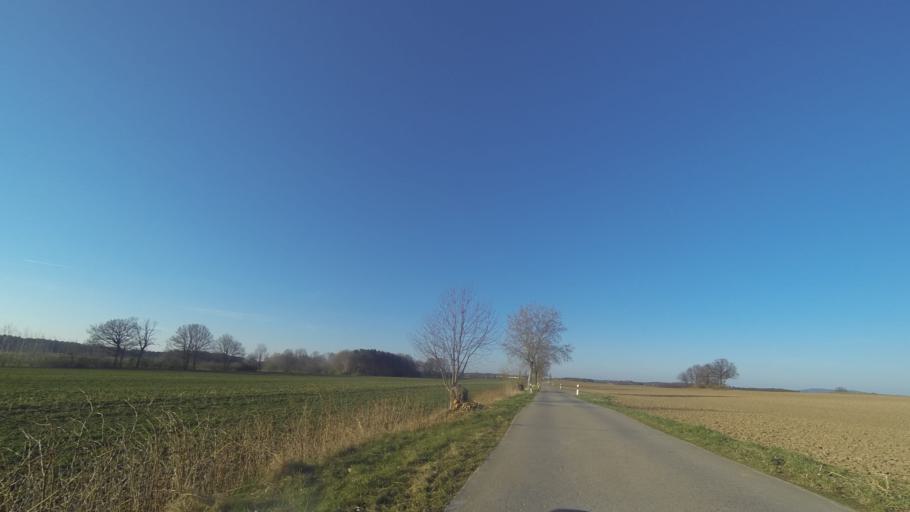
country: DE
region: Saxony
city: Radeburg
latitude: 51.1692
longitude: 13.7709
